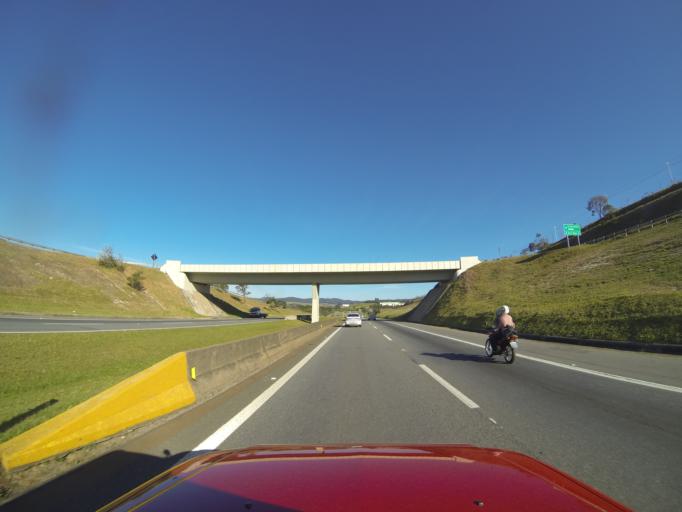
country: BR
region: Sao Paulo
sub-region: Bom Jesus Dos Perdoes
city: Bom Jesus dos Perdoes
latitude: -23.1577
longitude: -46.4503
